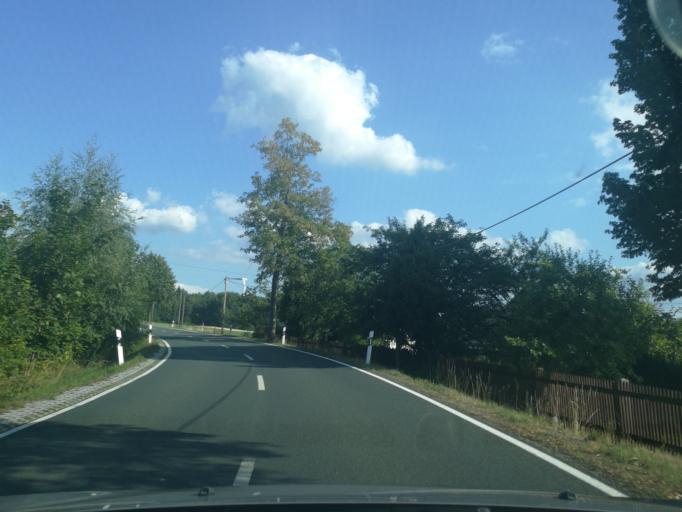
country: CZ
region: Karlovarsky
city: Hranice
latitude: 50.3242
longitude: 12.1579
